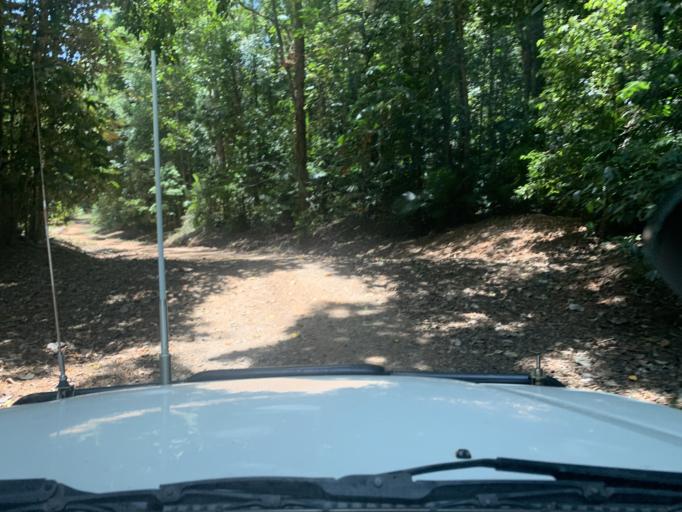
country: AU
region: Queensland
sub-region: Cairns
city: Redlynch
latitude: -16.9715
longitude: 145.6501
